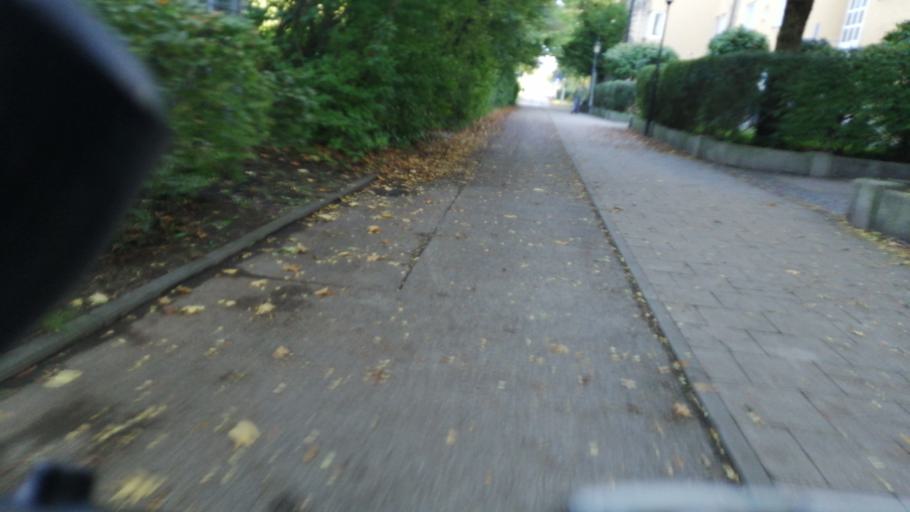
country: DE
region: Bavaria
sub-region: Upper Bavaria
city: Unterfoehring
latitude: 48.2051
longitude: 11.6070
